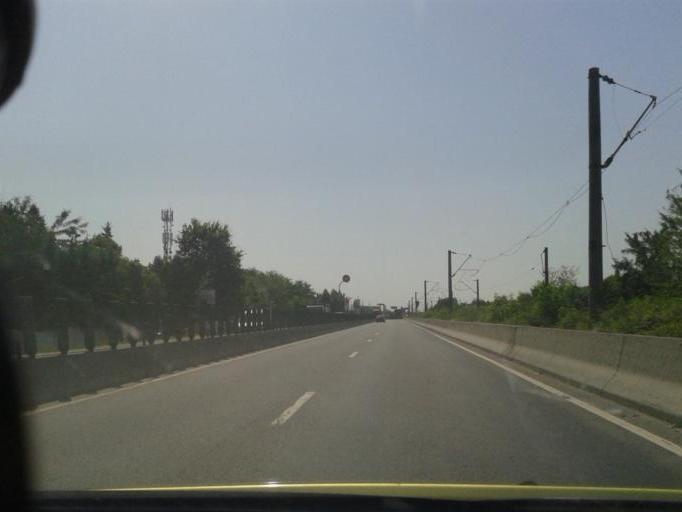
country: RO
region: Ilfov
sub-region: Voluntari City
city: Voluntari
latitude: 44.5060
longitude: 26.1958
